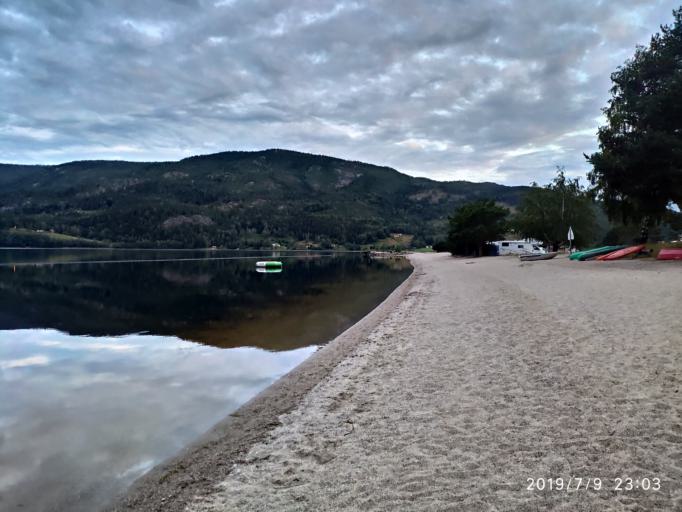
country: NO
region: Telemark
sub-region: Seljord
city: Seljord
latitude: 59.4856
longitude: 8.6523
